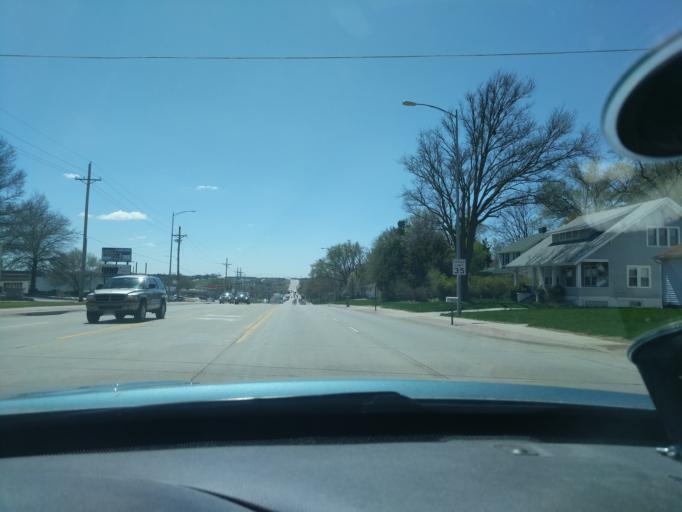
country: US
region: Nebraska
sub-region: Douglas County
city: Elkhorn
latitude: 41.2891
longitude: -96.2344
